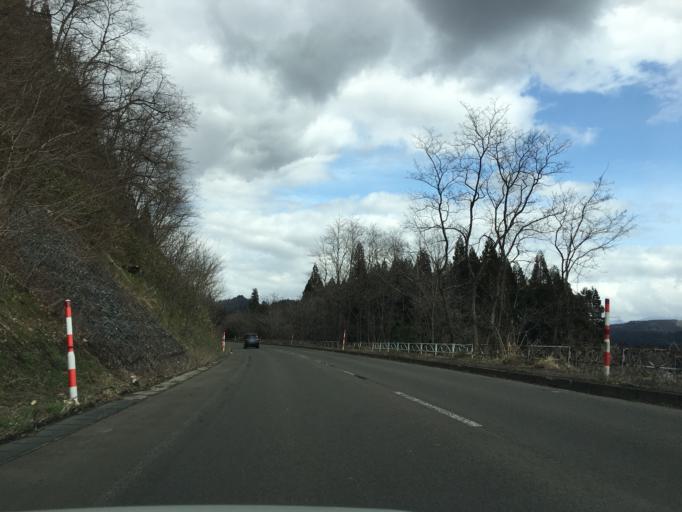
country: JP
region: Akita
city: Odate
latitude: 40.2187
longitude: 140.6461
